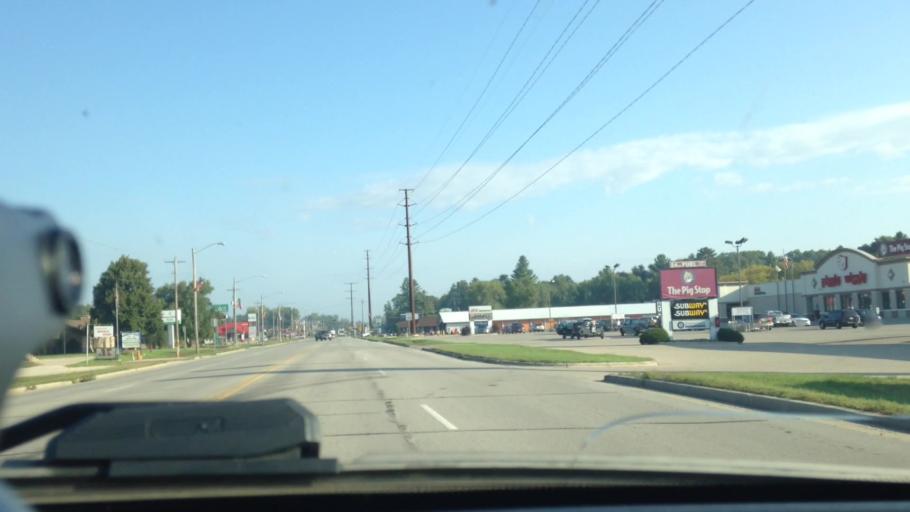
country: US
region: Wisconsin
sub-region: Marinette County
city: Peshtigo
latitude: 45.2276
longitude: -87.9967
